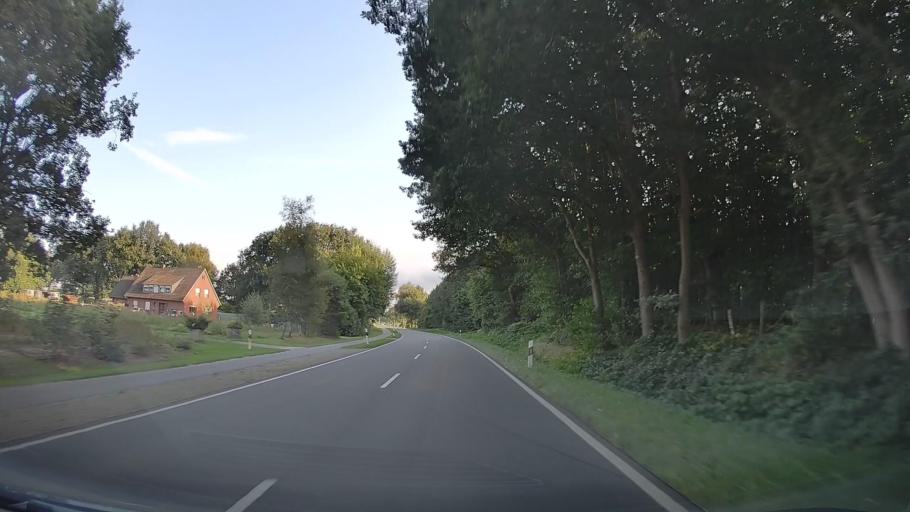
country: DE
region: Lower Saxony
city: Hilkenbrook
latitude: 53.0556
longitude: 7.7272
